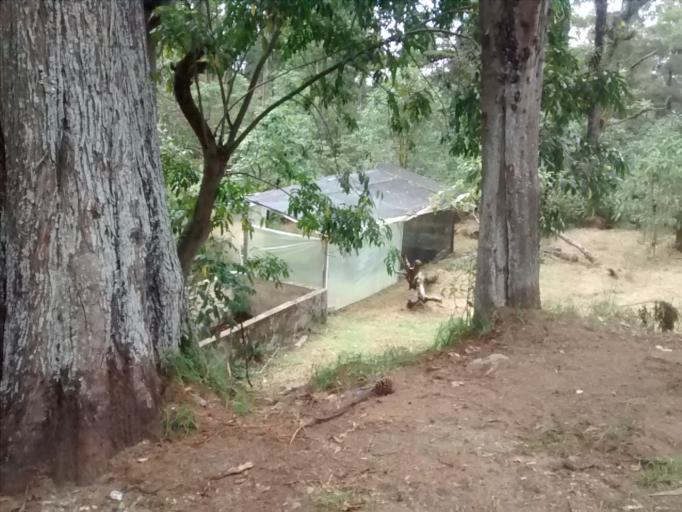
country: CO
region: Bogota D.C.
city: Bogota
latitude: 4.5977
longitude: -74.0620
